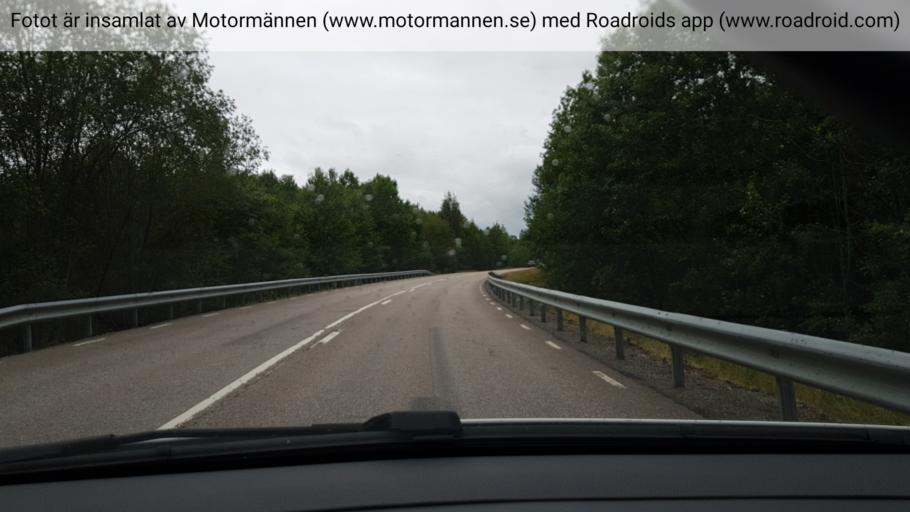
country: SE
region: Stockholm
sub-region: Vaxholms Kommun
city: Vaxholm
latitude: 59.3938
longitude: 18.4082
